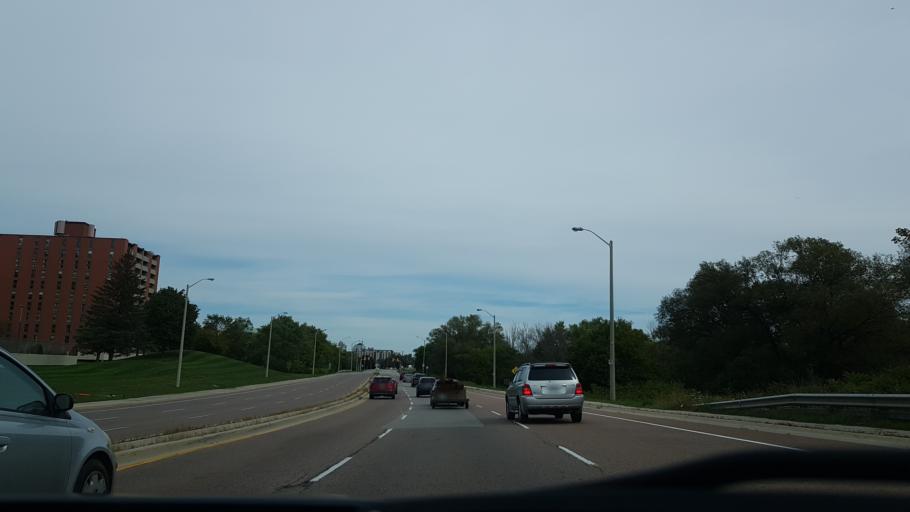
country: CA
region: Ontario
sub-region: Wellington County
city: Guelph
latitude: 43.5290
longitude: -80.2605
